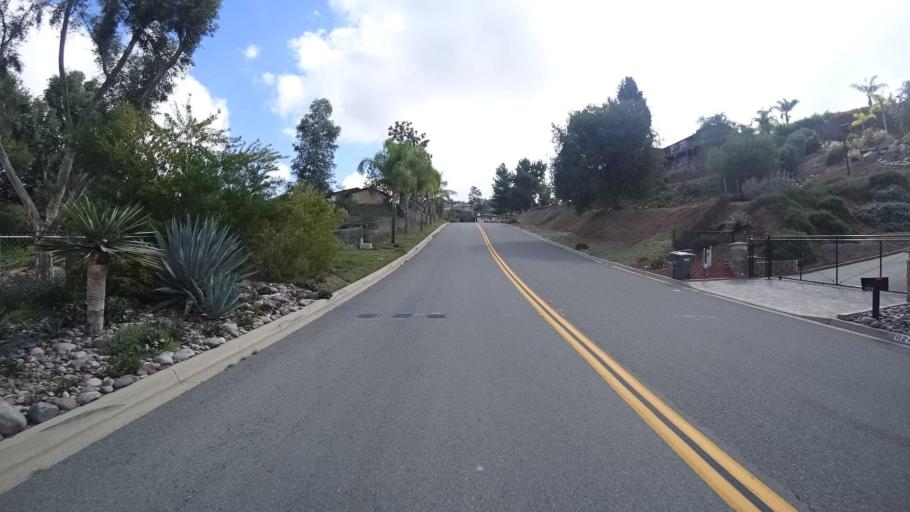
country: US
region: California
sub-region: San Diego County
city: Granite Hills
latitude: 32.7768
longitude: -116.9016
